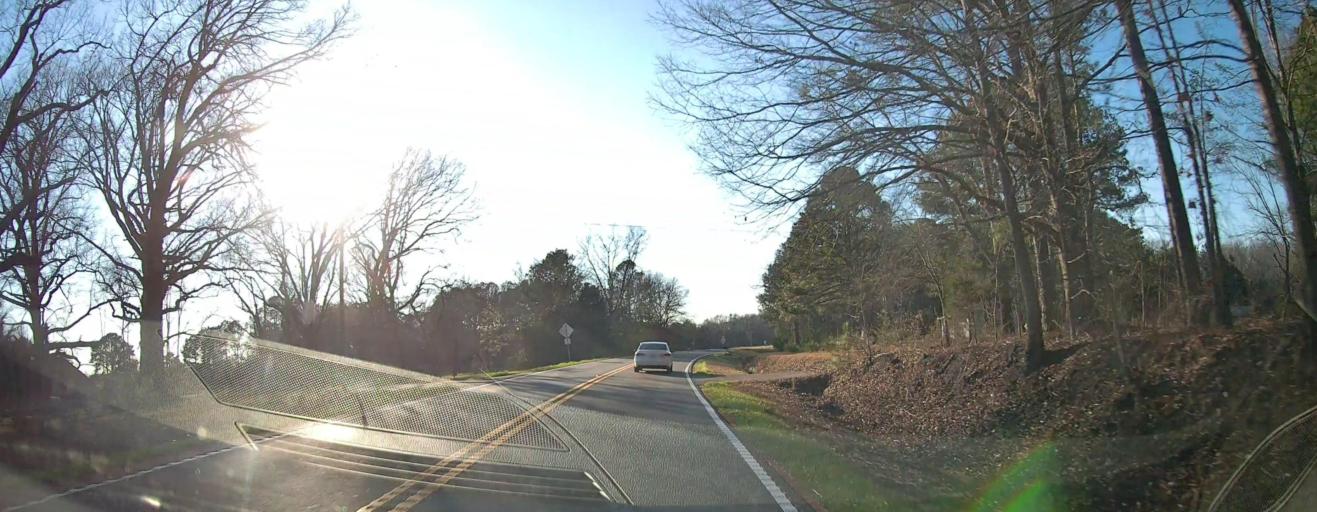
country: US
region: Georgia
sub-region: Meriwether County
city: Greenville
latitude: 32.9116
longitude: -84.7373
